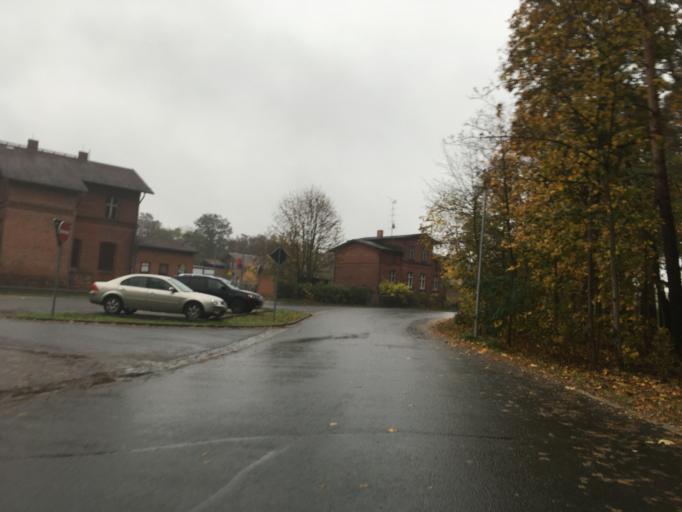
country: DE
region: Brandenburg
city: Halbe
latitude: 52.0298
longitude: 13.7205
